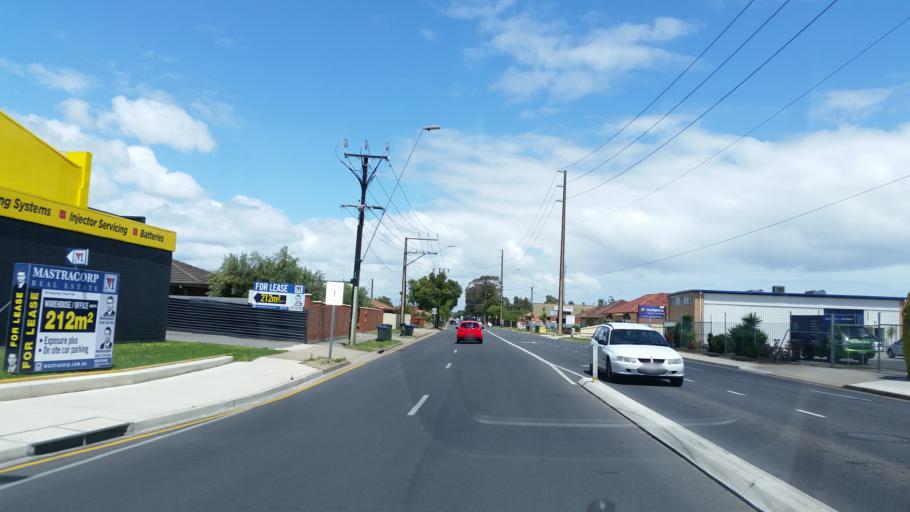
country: AU
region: South Australia
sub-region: Charles Sturt
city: Findon
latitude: -34.9057
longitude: 138.5327
